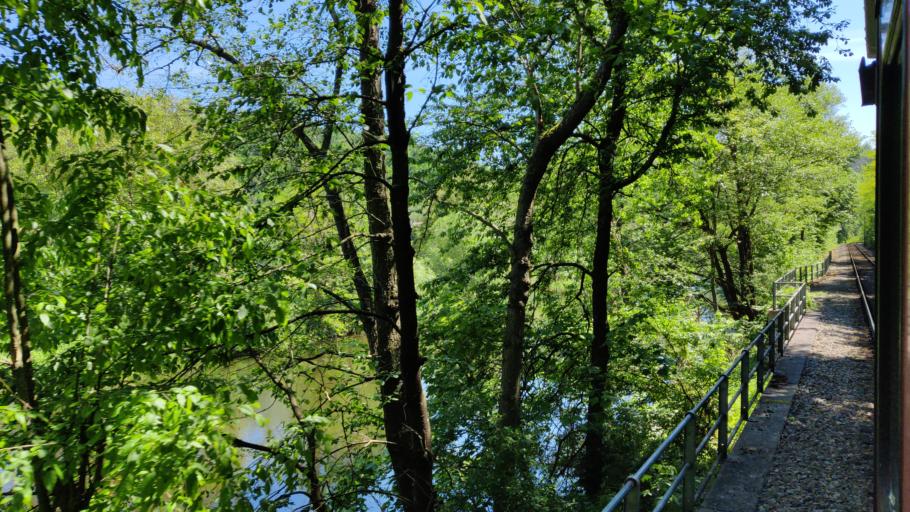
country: AT
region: Lower Austria
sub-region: Politischer Bezirk Horn
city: Gars am Kamp
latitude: 48.6113
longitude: 15.6526
